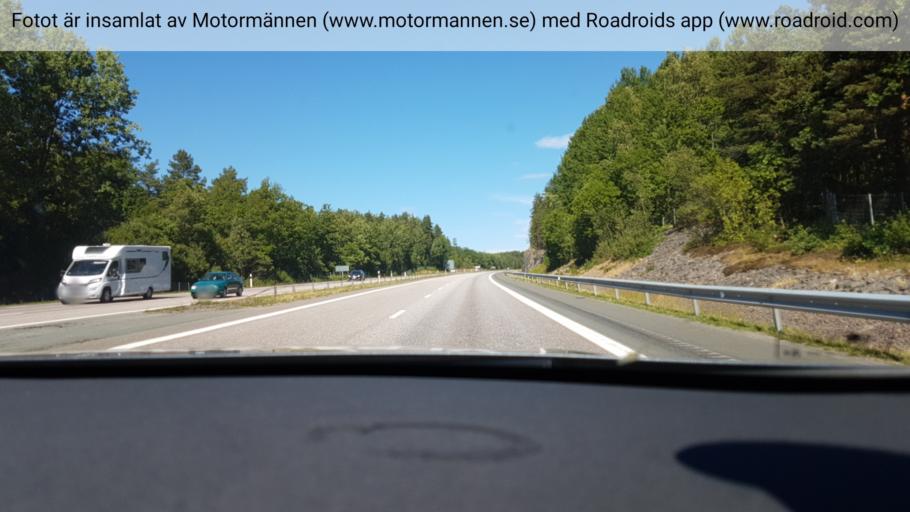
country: SE
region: Joenkoeping
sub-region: Jonkopings Kommun
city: Graenna
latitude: 58.0095
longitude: 14.4655
